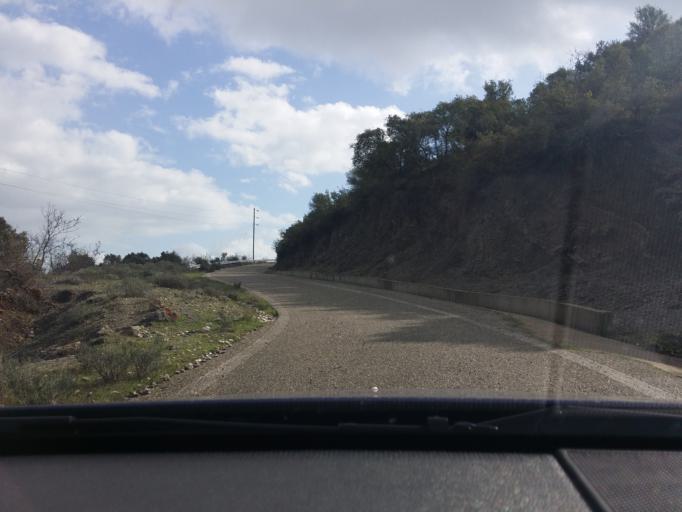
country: GR
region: West Greece
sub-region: Nomos Aitolias kai Akarnanias
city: Fitiai
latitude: 38.6577
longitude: 21.1963
